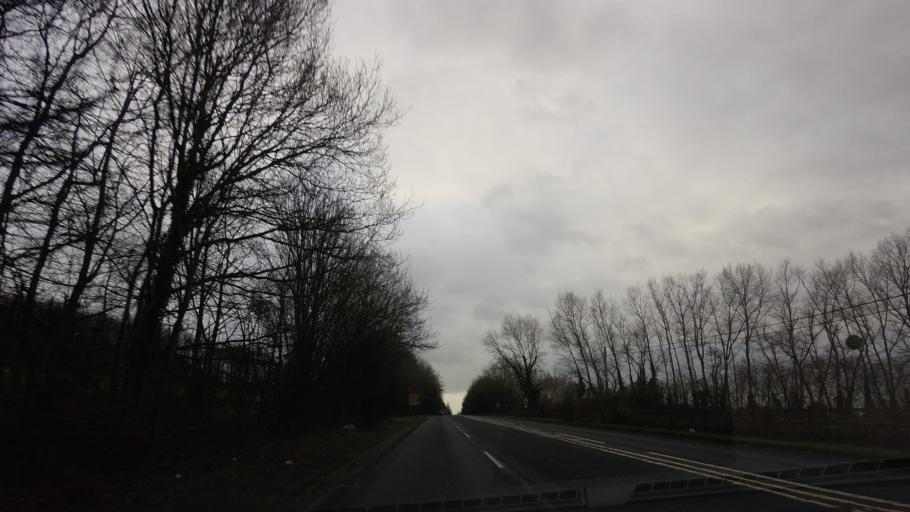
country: GB
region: England
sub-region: Kent
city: East Peckham
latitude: 51.2468
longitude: 0.3750
